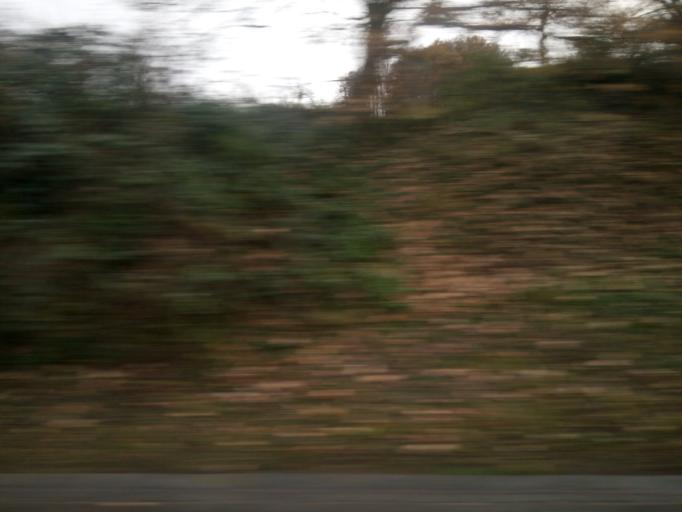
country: LU
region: Diekirch
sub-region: Canton de Vianden
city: Tandel
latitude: 49.8955
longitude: 6.1818
